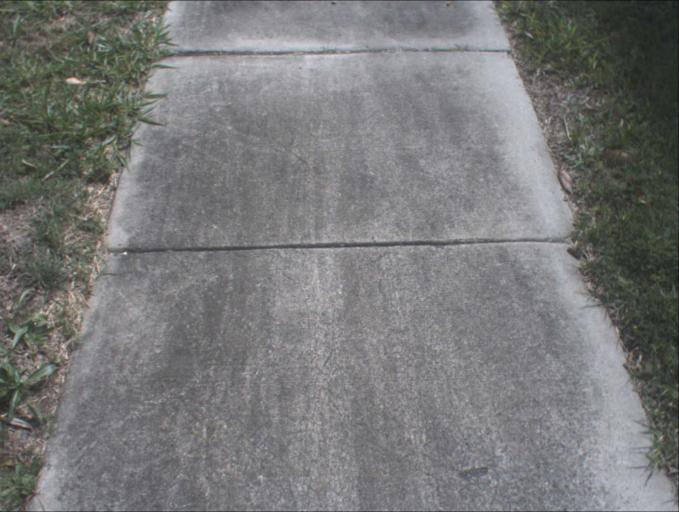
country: AU
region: Queensland
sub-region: Logan
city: Woodridge
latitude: -27.6686
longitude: 153.0843
